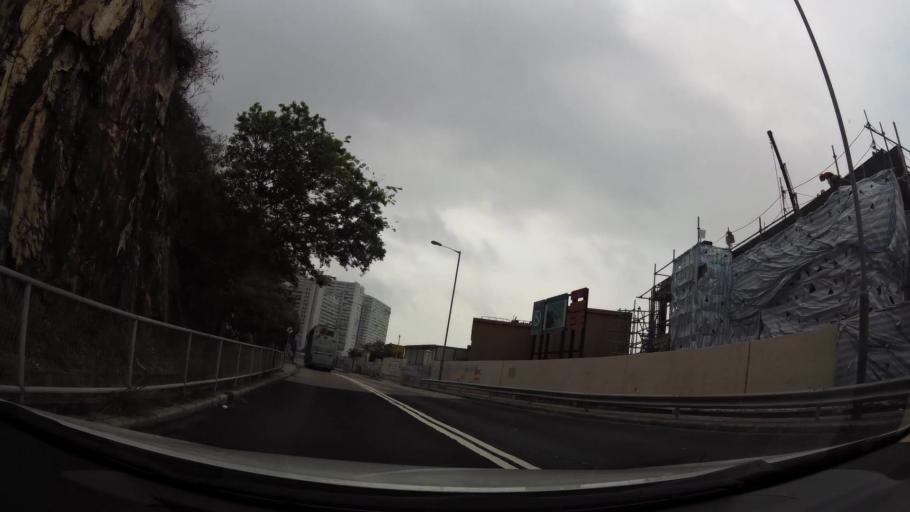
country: HK
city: Yung Shue Wan
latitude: 22.2399
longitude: 114.1486
